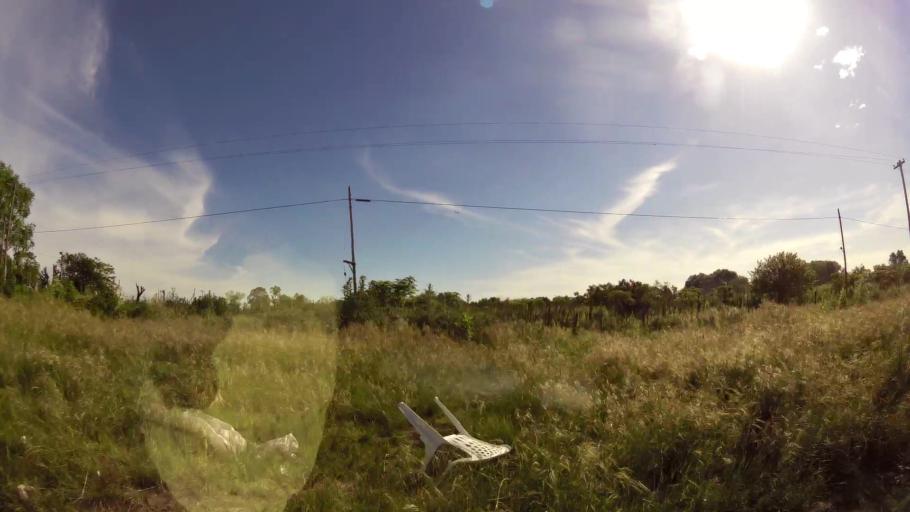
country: AR
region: Buenos Aires
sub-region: Partido de Almirante Brown
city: Adrogue
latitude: -34.8246
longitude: -58.3376
